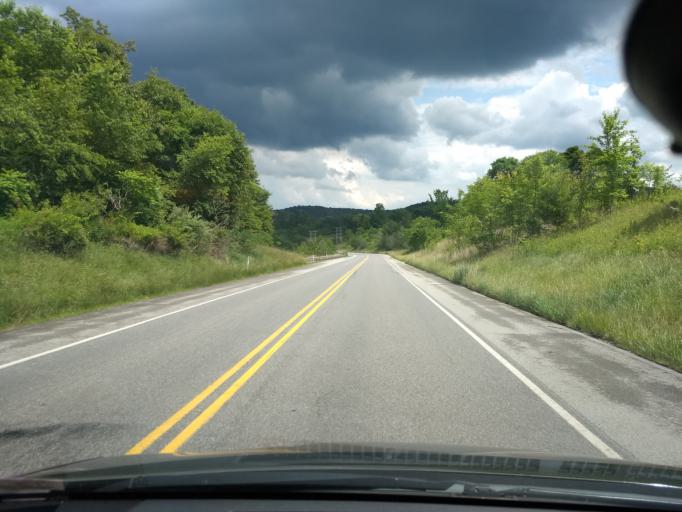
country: US
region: Pennsylvania
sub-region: Westmoreland County
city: Avonmore
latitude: 40.5187
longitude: -79.5009
